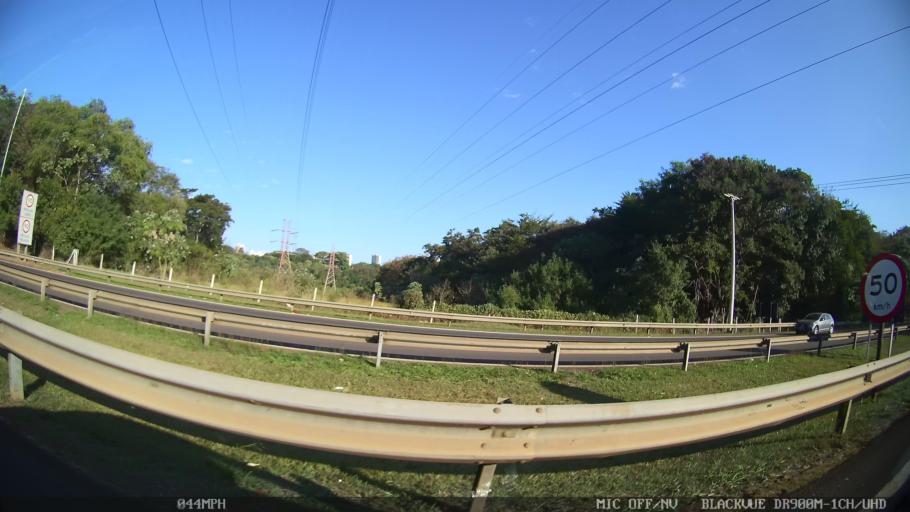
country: BR
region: Sao Paulo
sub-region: Piracicaba
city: Piracicaba
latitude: -22.7020
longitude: -47.6447
